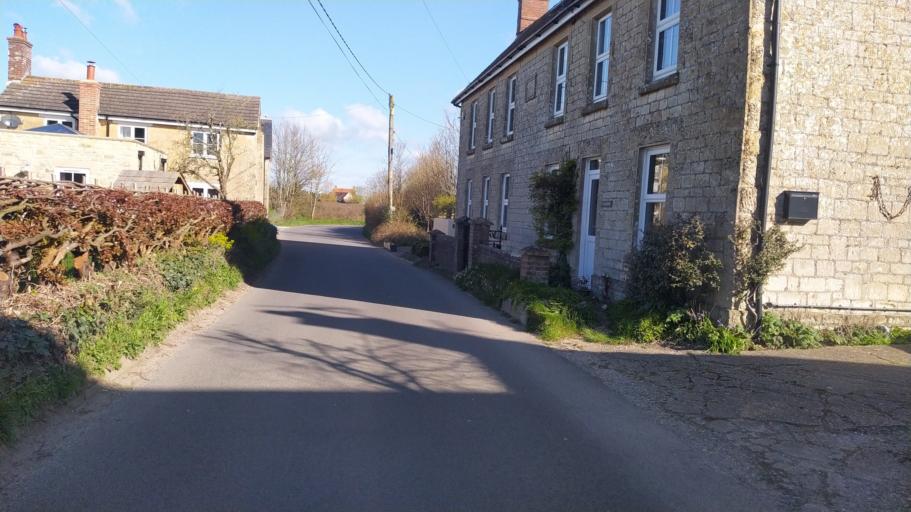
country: GB
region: England
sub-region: Dorset
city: Sturminster Newton
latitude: 50.9594
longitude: -2.3253
